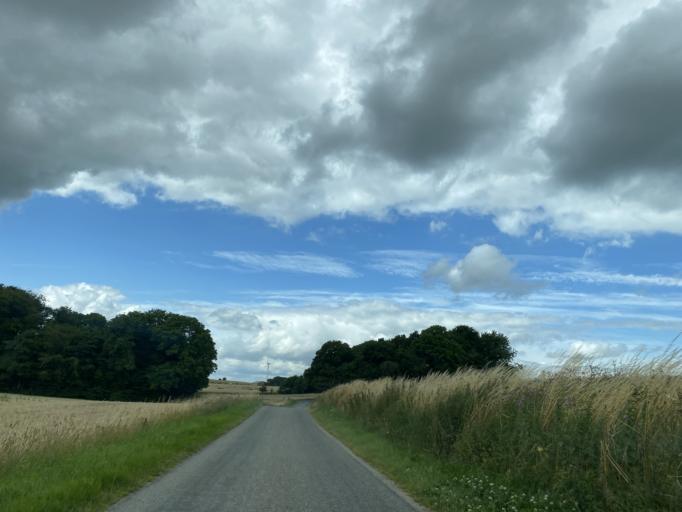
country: DK
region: Central Jutland
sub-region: Silkeborg Kommune
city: Svejbaek
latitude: 56.2366
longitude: 9.6501
